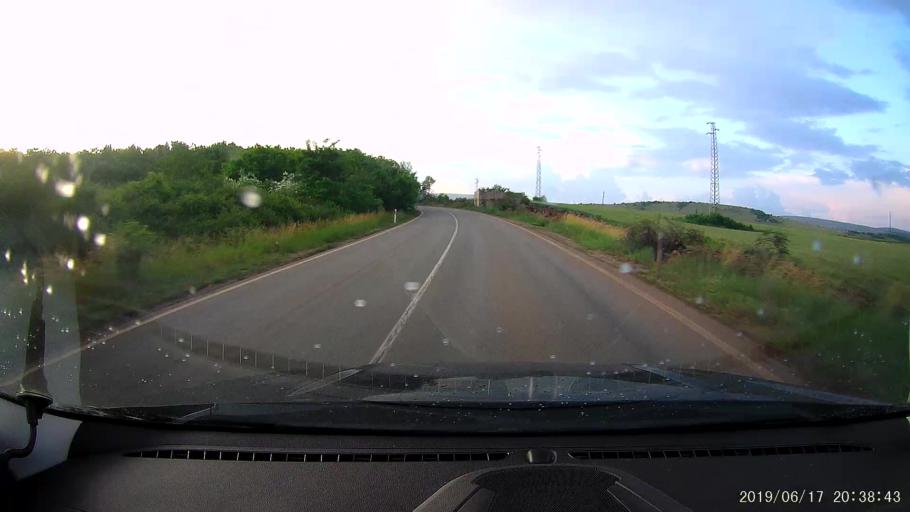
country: BG
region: Sofiya
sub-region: Obshtina Slivnitsa
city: Slivnitsa
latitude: 42.8764
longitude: 23.0186
